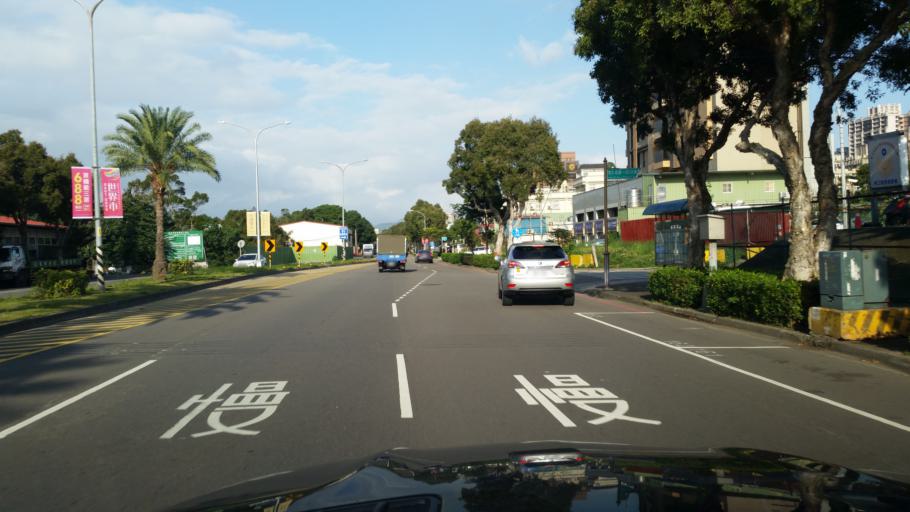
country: TW
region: Taiwan
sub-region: Taoyuan
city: Taoyuan
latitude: 25.0791
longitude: 121.3673
